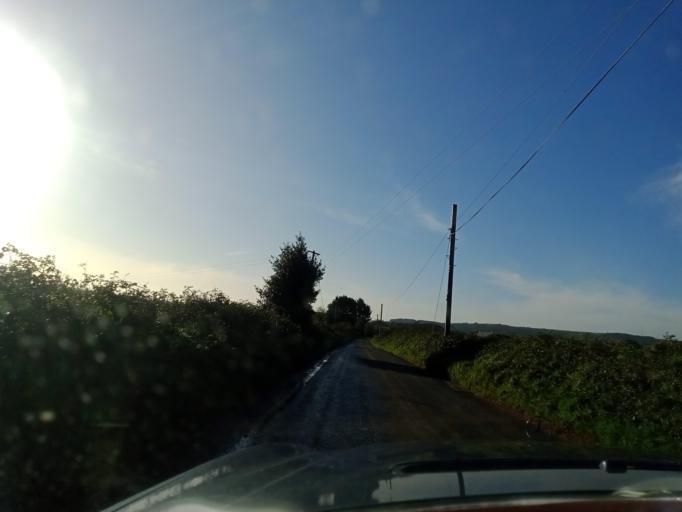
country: IE
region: Leinster
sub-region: Kilkenny
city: Mooncoin
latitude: 52.2832
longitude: -7.2371
